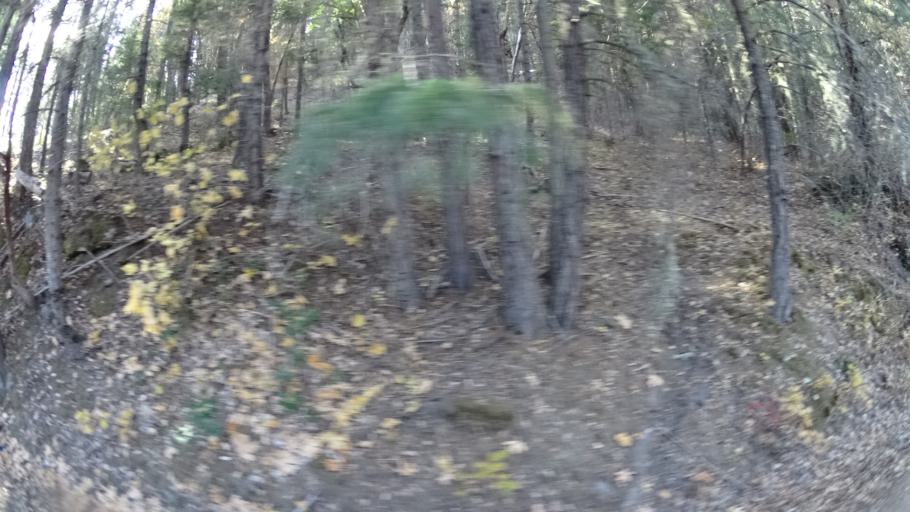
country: US
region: California
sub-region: Siskiyou County
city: Yreka
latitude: 41.8449
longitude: -122.9014
